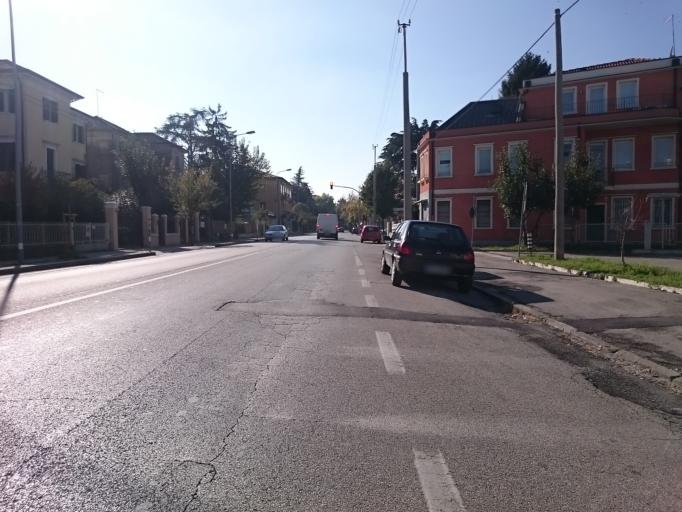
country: IT
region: Veneto
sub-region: Provincia di Padova
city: Padova
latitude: 45.4019
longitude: 11.8589
